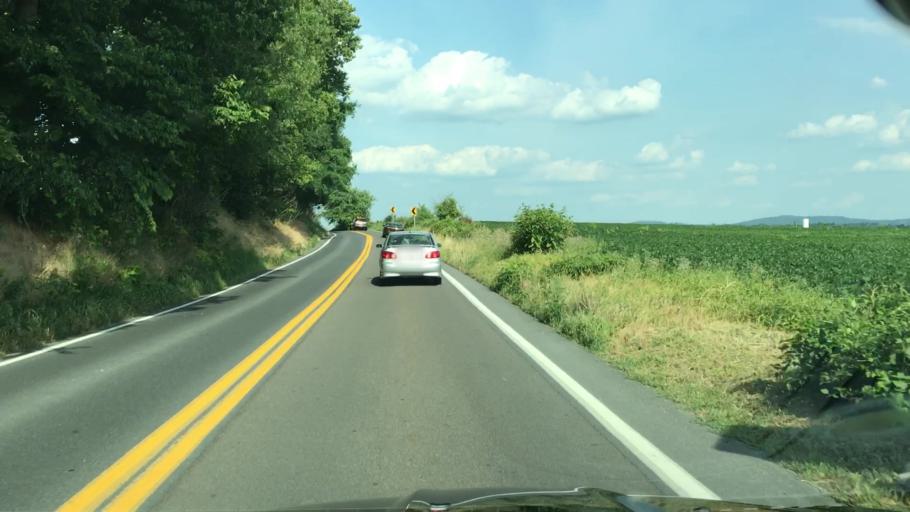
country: US
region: Pennsylvania
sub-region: York County
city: Dillsburg
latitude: 40.1607
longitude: -77.0216
